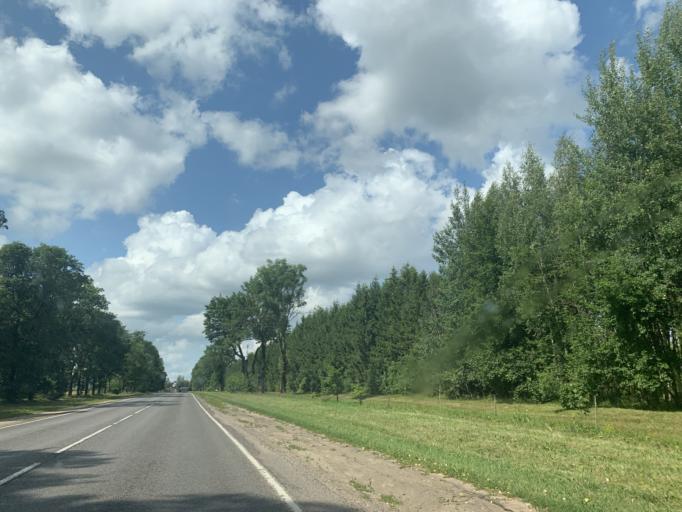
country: BY
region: Minsk
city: Enyerhyetykaw
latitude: 53.5800
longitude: 27.0562
